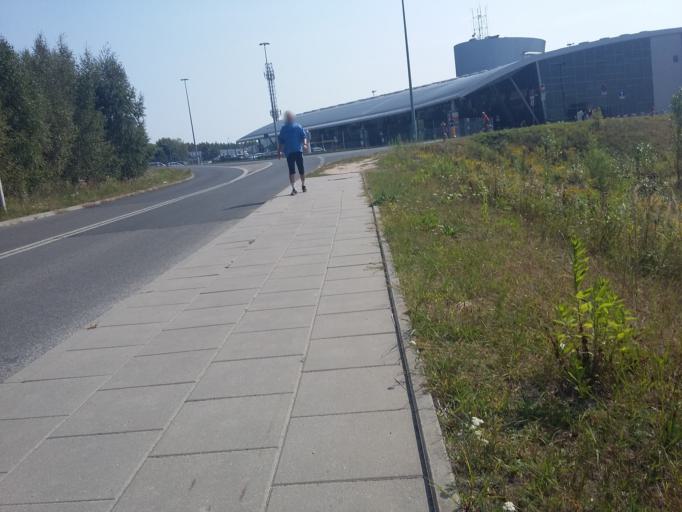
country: PL
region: Lodz Voivodeship
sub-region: Powiat pabianicki
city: Ksawerow
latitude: 51.7278
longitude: 19.3988
